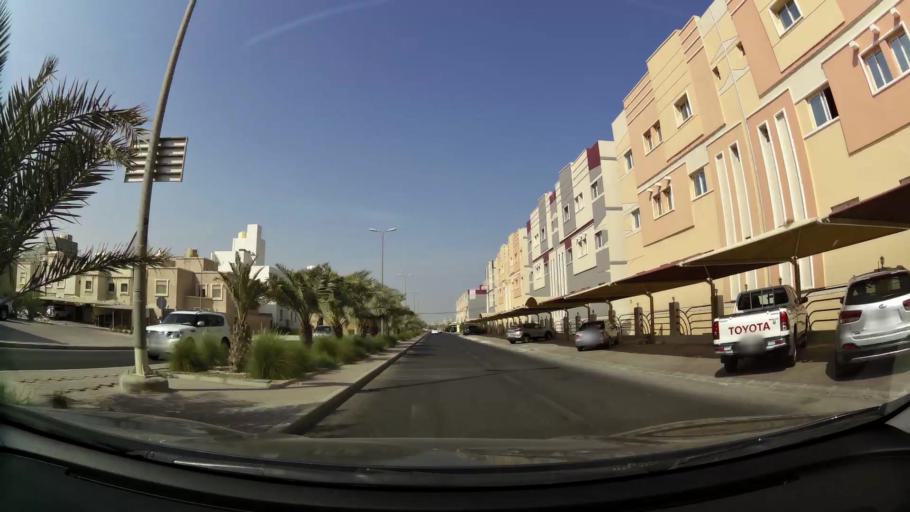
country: KW
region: Al Ahmadi
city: Al Manqaf
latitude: 29.1140
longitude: 48.1228
